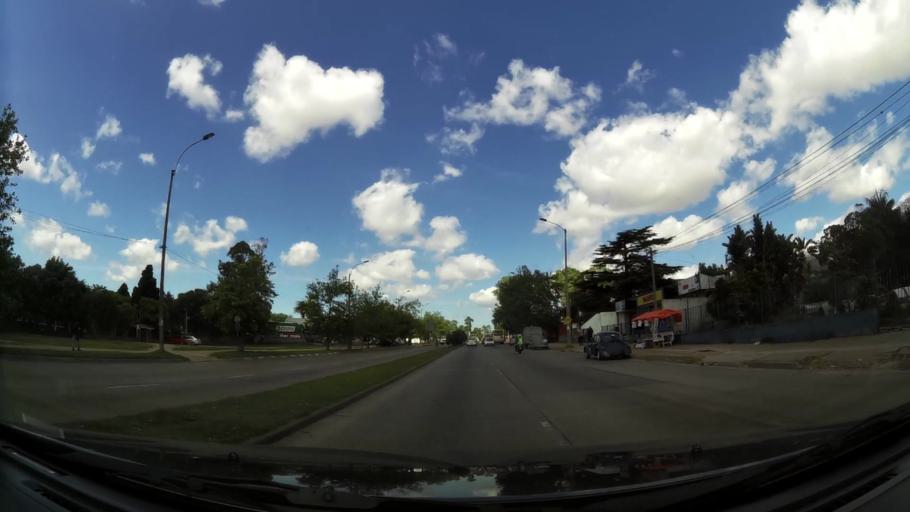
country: UY
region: Canelones
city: Paso de Carrasco
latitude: -34.8405
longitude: -56.1224
